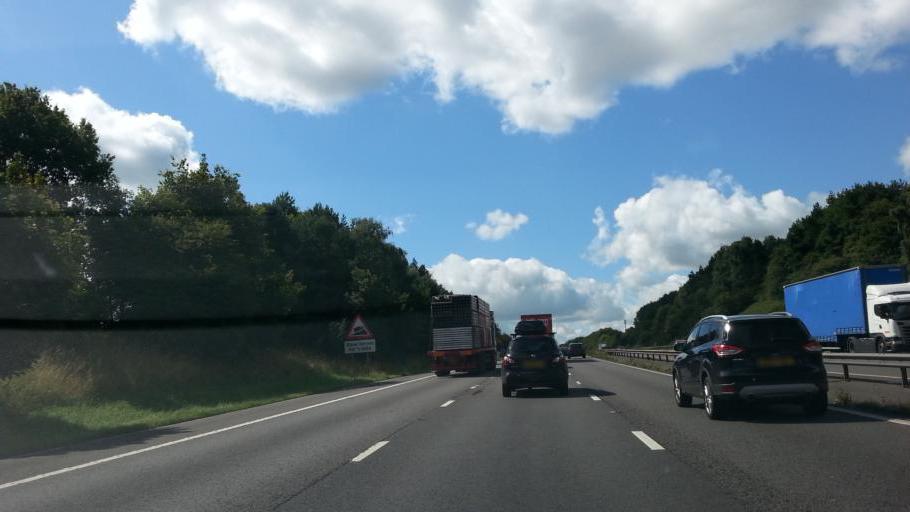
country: GB
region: England
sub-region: Leicestershire
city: Markfield
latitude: 52.7180
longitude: -1.2859
